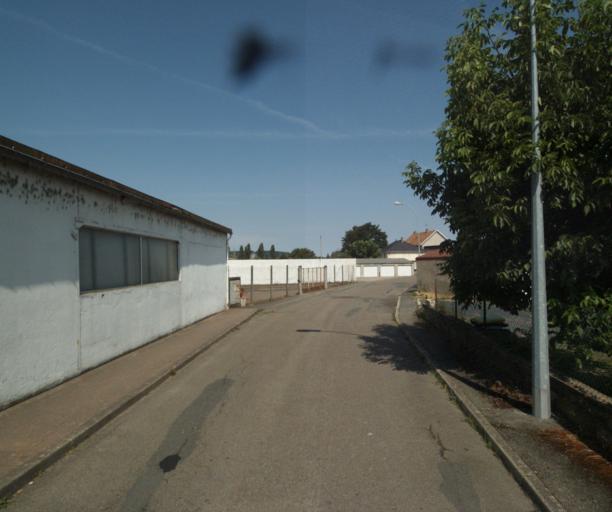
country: FR
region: Bourgogne
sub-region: Departement de Saone-et-Loire
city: Gueugnon
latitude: 46.5960
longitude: 4.0666
